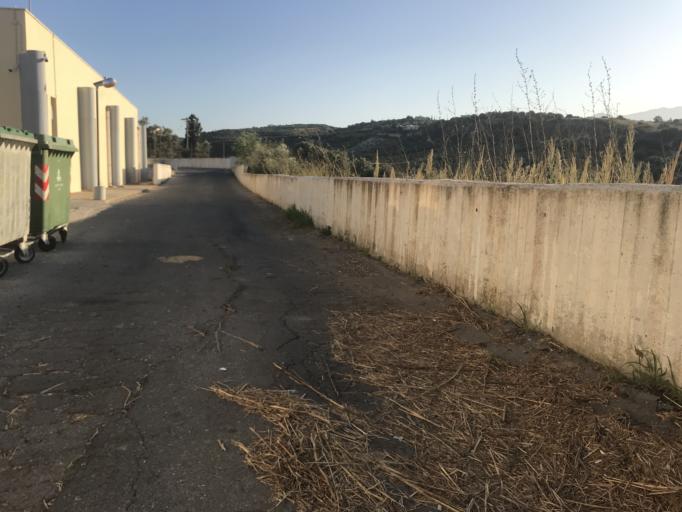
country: GR
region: Crete
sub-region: Nomos Irakleiou
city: Gazi
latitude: 35.3052
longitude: 25.0705
